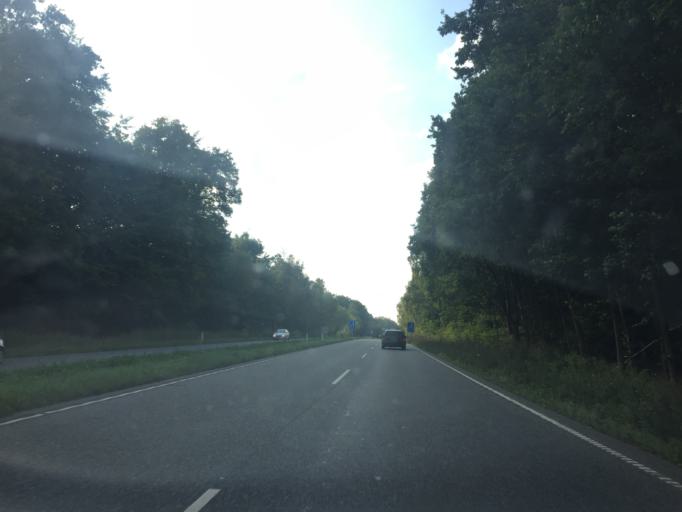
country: DK
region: Zealand
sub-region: Holbaek Kommune
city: Jyderup
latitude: 55.6637
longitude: 11.4028
